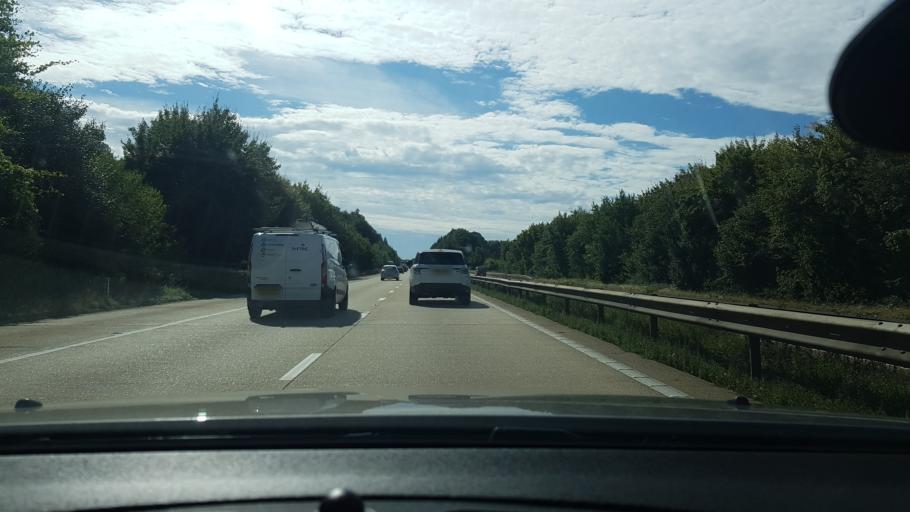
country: GB
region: England
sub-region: Hampshire
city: Kings Worthy
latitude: 51.1354
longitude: -1.2471
